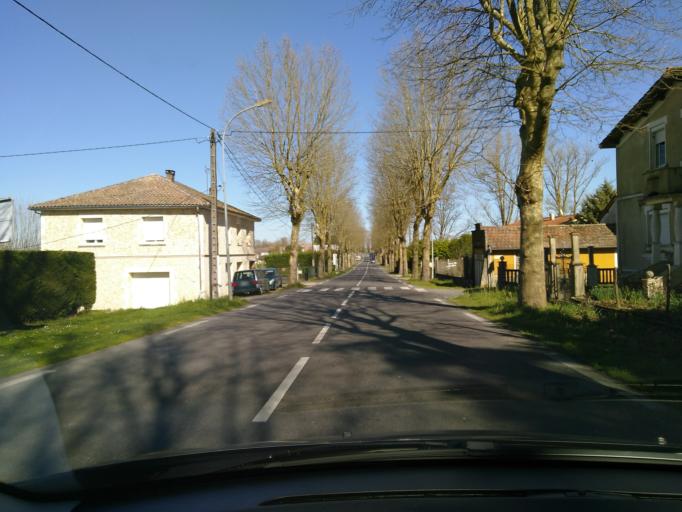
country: FR
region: Aquitaine
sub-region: Departement du Lot-et-Garonne
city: Cancon
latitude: 44.5406
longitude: 0.6230
